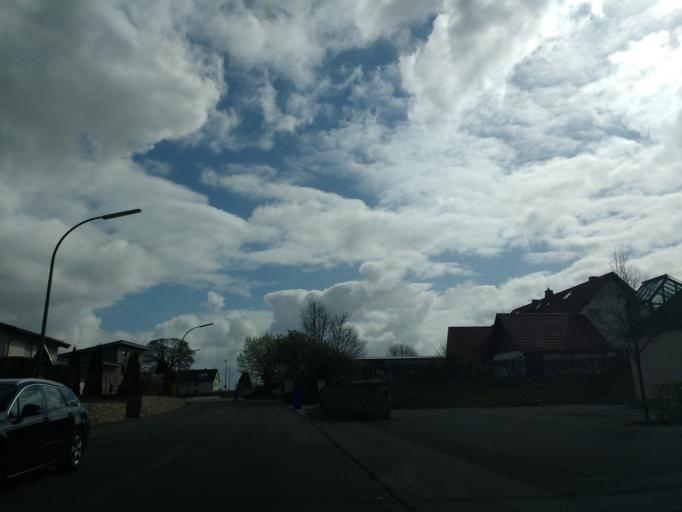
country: DE
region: North Rhine-Westphalia
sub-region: Regierungsbezirk Detmold
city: Wunnenberg
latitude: 51.5163
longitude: 8.7452
